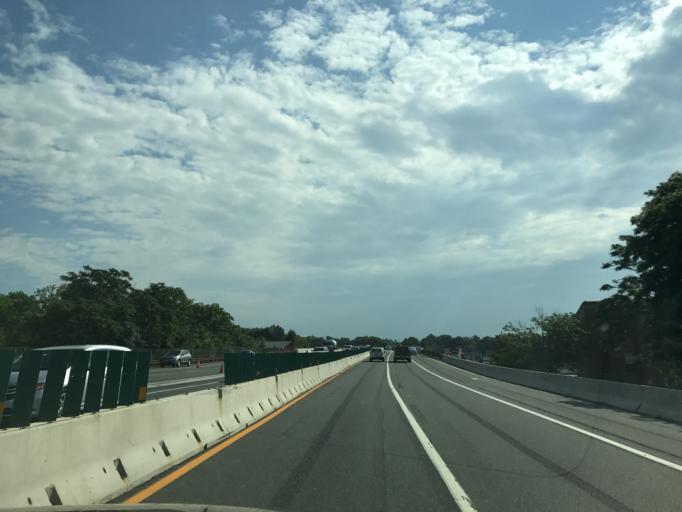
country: US
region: New Jersey
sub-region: Essex County
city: Glen Ridge
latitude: 40.7886
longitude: -74.1974
